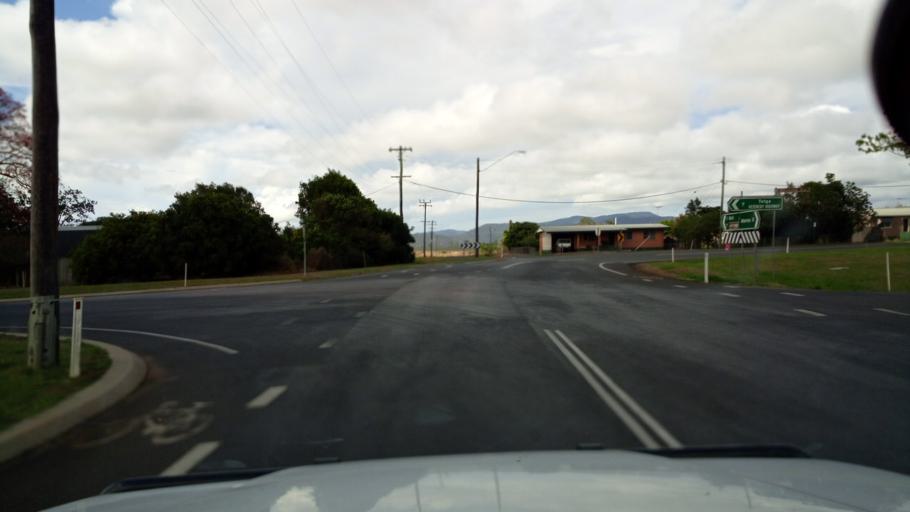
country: AU
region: Queensland
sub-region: Tablelands
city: Tolga
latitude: -17.2163
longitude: 145.5381
